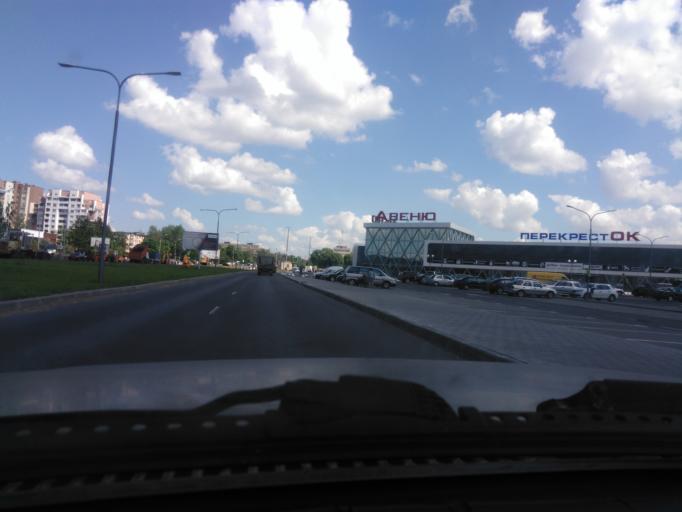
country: BY
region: Mogilev
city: Mahilyow
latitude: 53.9189
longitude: 30.2991
